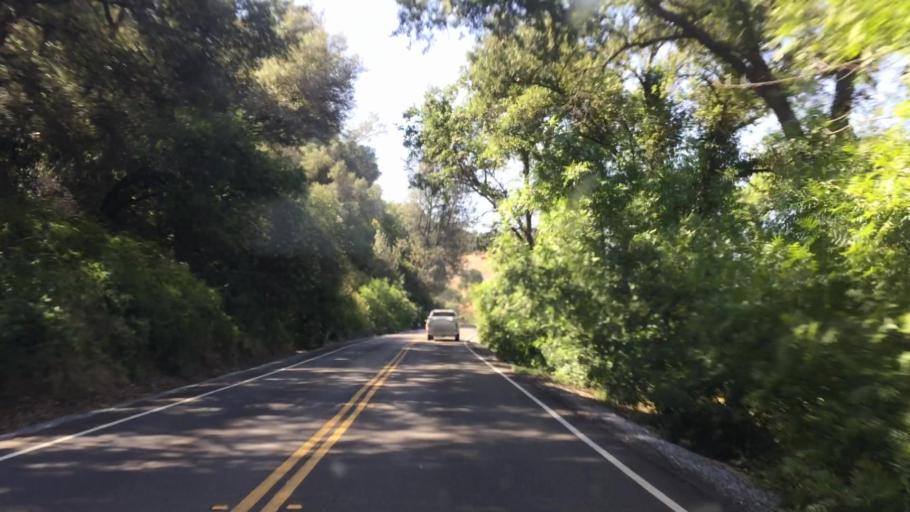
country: US
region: California
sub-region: Amador County
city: Plymouth
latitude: 38.5201
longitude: -120.9542
